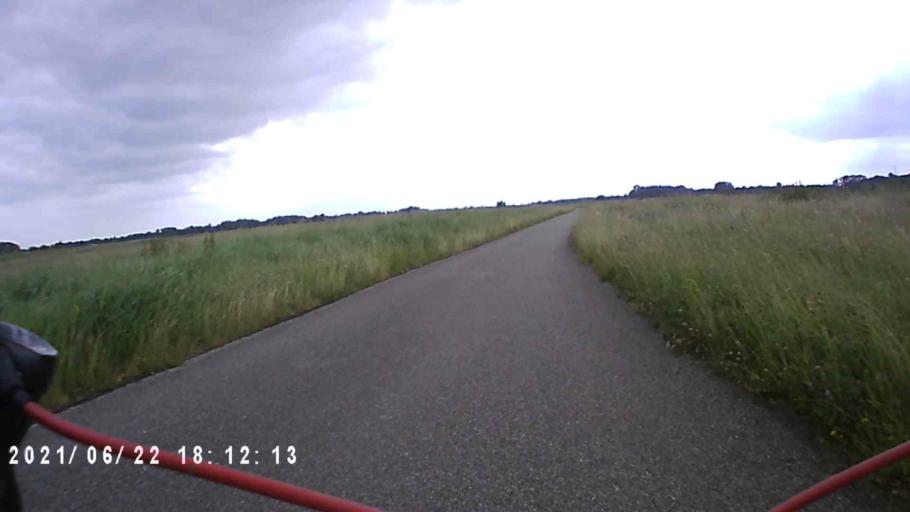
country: NL
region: Groningen
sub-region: Gemeente Zuidhorn
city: Aduard
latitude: 53.1771
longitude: 6.4916
